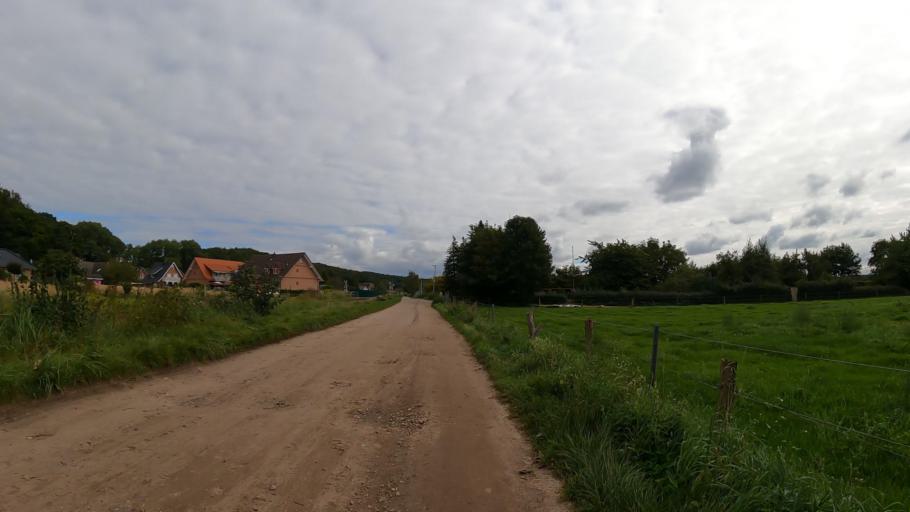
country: DE
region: Schleswig-Holstein
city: Escheburg
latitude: 53.4597
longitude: 10.3251
